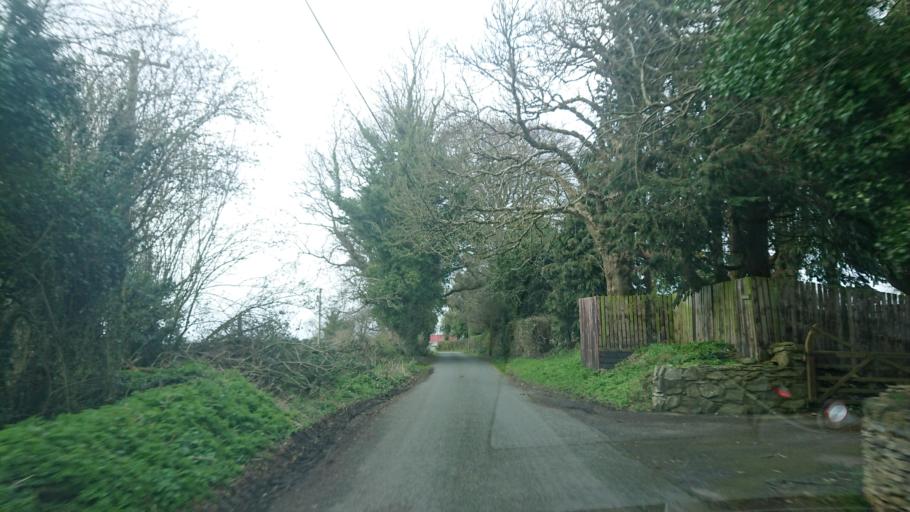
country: IE
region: Leinster
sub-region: Kildare
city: Eadestown
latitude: 53.1642
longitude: -6.6072
